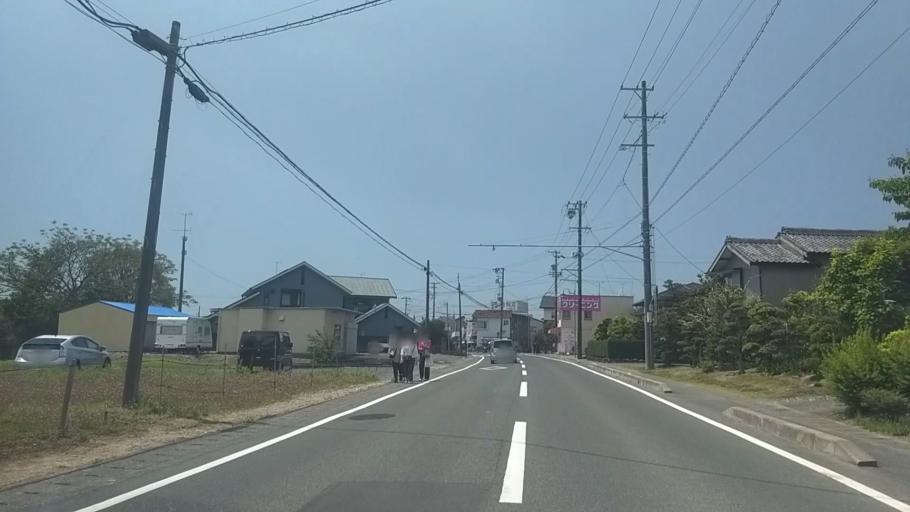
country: JP
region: Shizuoka
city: Hamamatsu
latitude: 34.7644
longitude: 137.6588
